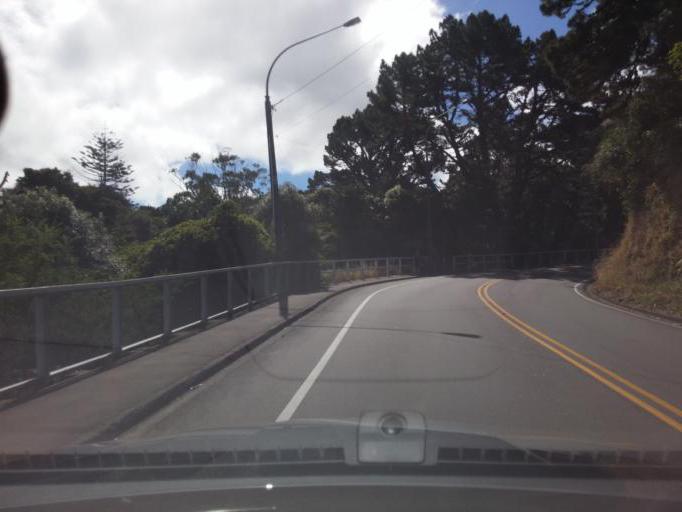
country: NZ
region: Wellington
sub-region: Wellington City
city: Kelburn
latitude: -41.2571
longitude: 174.7734
